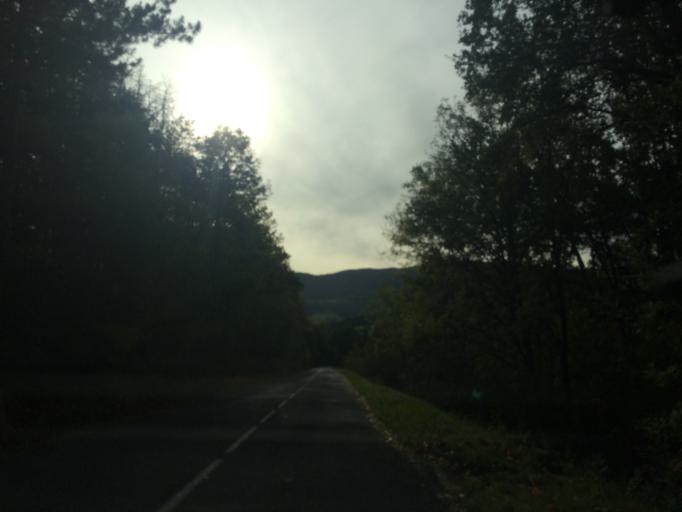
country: FR
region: Rhone-Alpes
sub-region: Departement de la Loire
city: Saint-Jean-Bonnefonds
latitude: 45.4563
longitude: 4.4545
